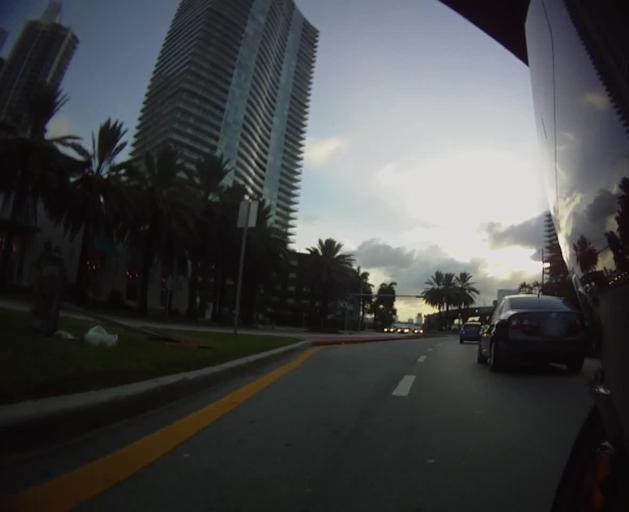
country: US
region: Florida
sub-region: Miami-Dade County
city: Miami Beach
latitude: 25.7744
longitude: -80.1399
